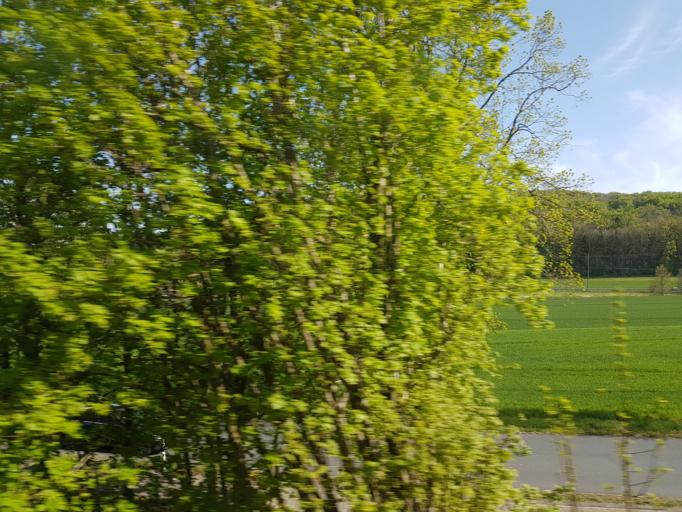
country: DE
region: Lower Saxony
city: Springe
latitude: 52.2020
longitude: 9.5315
